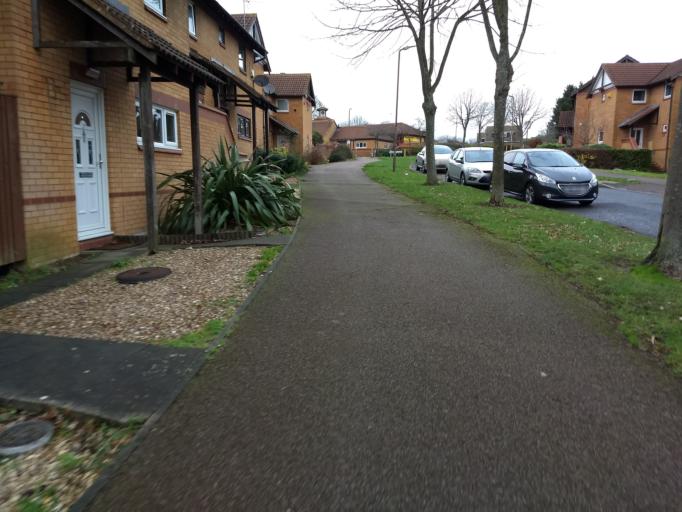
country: GB
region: England
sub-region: Buckinghamshire
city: Newton Longville
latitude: 51.9882
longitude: -0.7688
